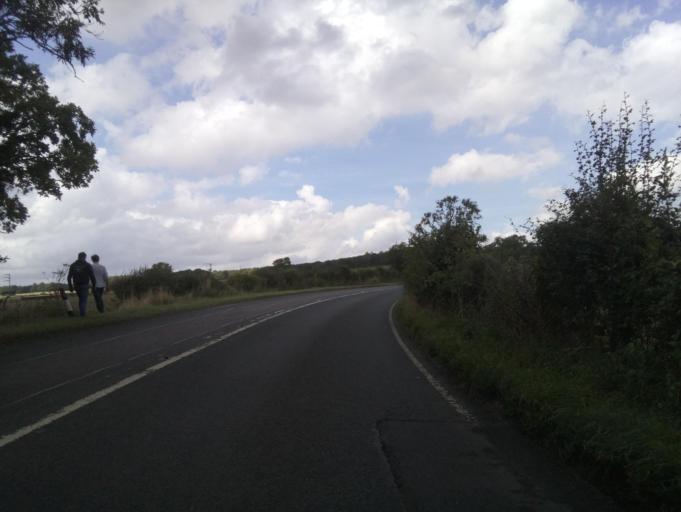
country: GB
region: England
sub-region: North Yorkshire
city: Catterick Garrison
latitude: 54.4294
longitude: -1.6812
